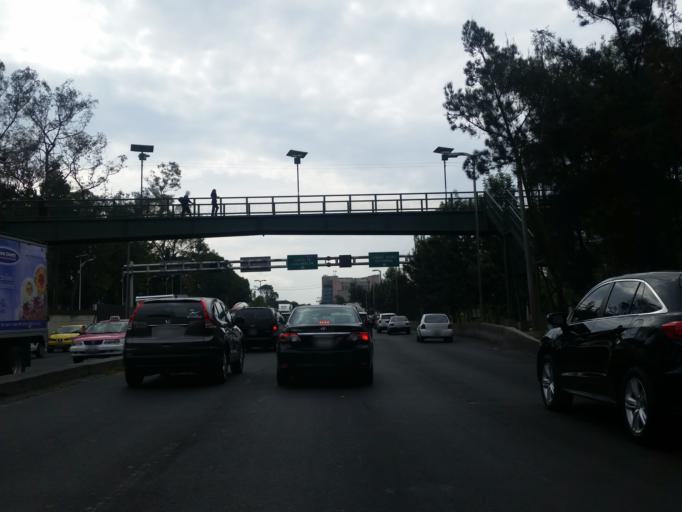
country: MX
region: Mexico City
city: Polanco
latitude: 19.3971
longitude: -99.2200
